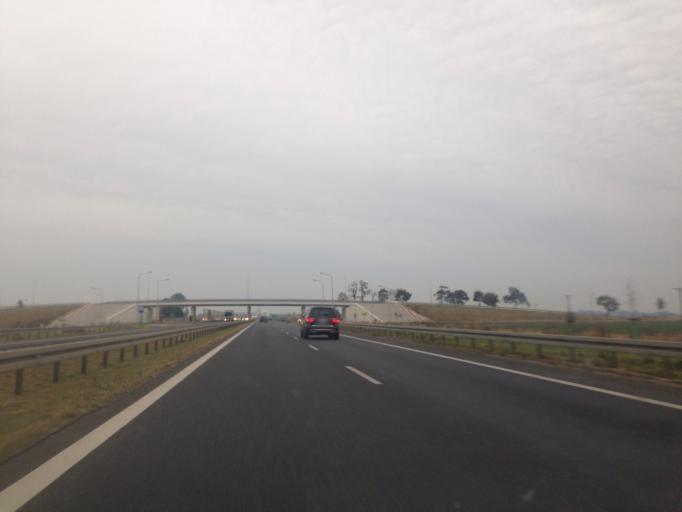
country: PL
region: Greater Poland Voivodeship
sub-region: Powiat gnieznienski
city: Gniezno
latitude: 52.5275
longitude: 17.5310
